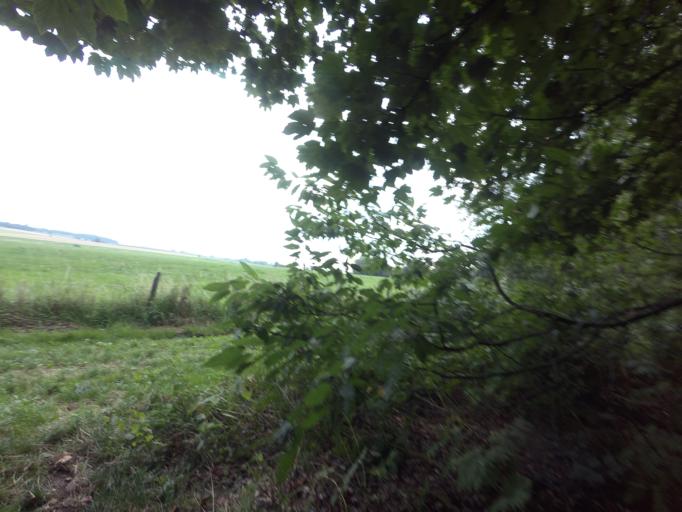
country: NL
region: Limburg
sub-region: Gemeente Vaals
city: Vaals
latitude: 50.7872
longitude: 6.0177
